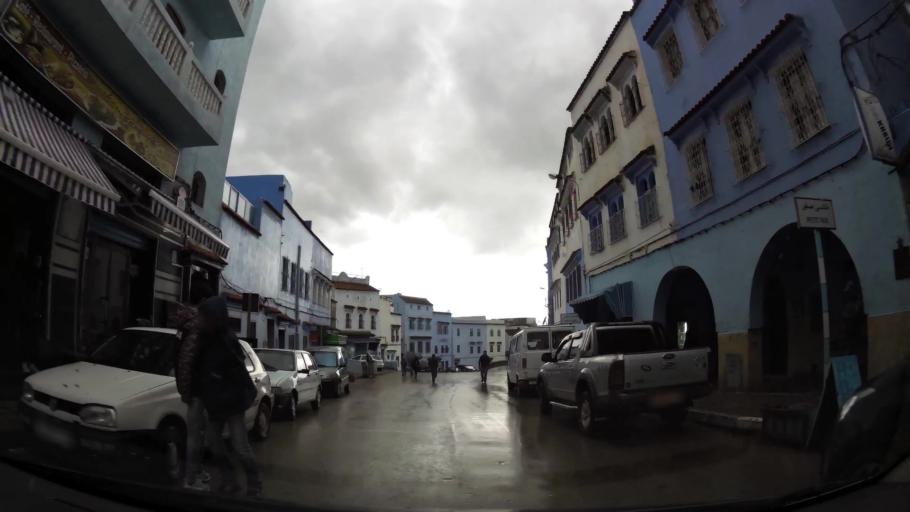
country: MA
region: Tanger-Tetouan
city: Chefchaouene
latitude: 35.1697
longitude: -5.2661
